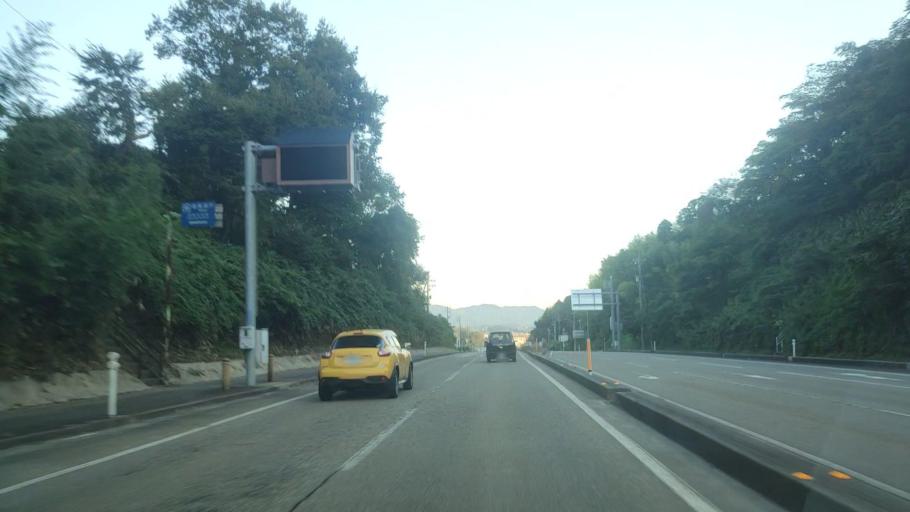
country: JP
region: Toyama
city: Himi
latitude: 36.8503
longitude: 136.9786
